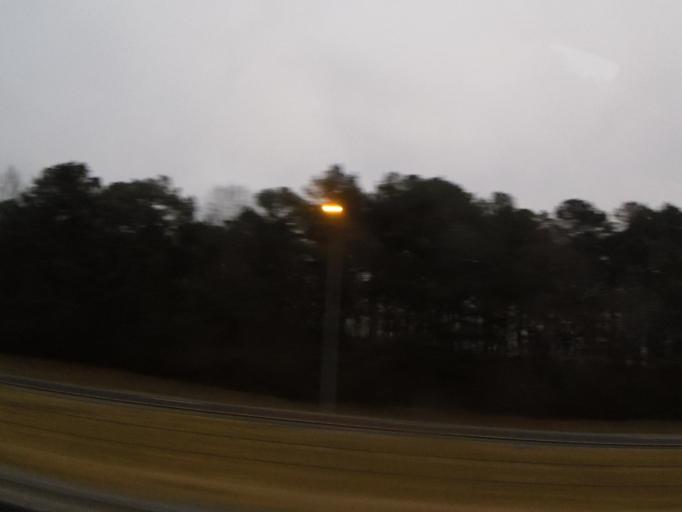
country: US
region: Alabama
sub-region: Cullman County
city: Cullman
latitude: 34.1734
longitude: -86.8759
